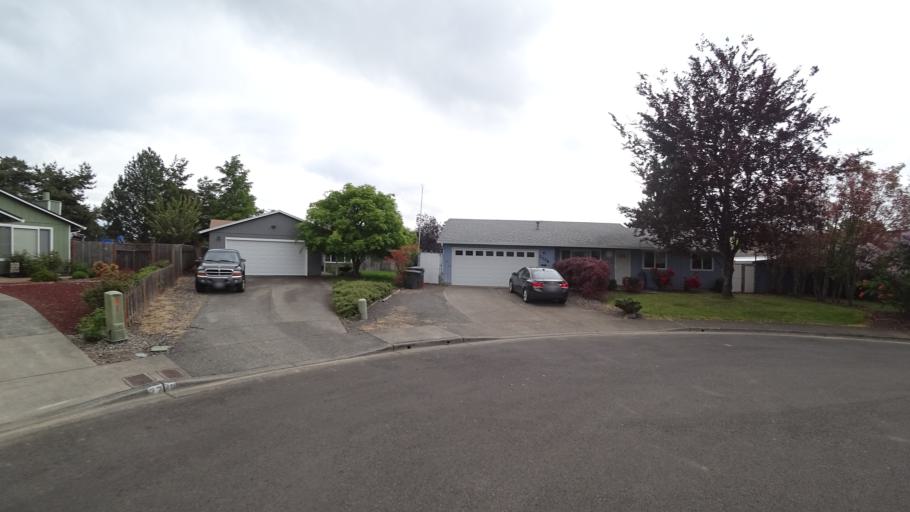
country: US
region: Oregon
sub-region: Washington County
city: Hillsboro
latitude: 45.5406
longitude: -122.9770
